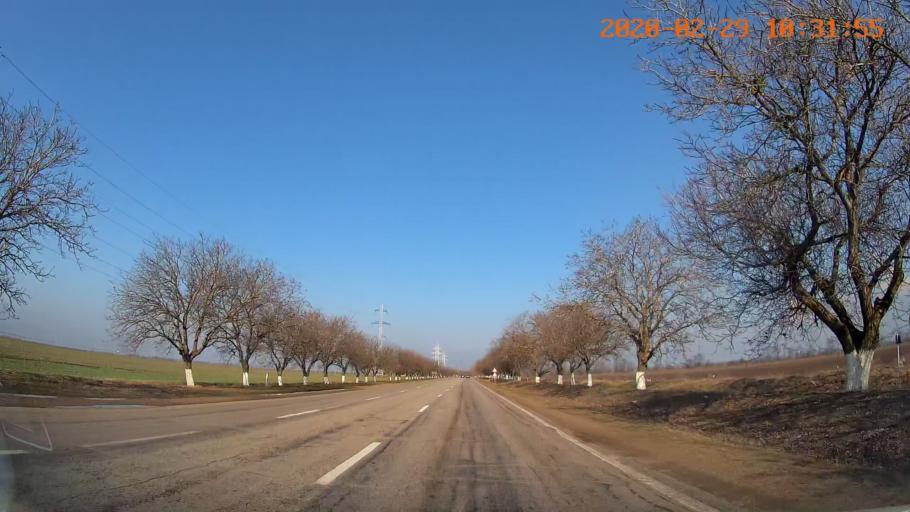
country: UA
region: Odessa
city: Velykoploske
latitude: 46.9545
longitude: 29.5586
